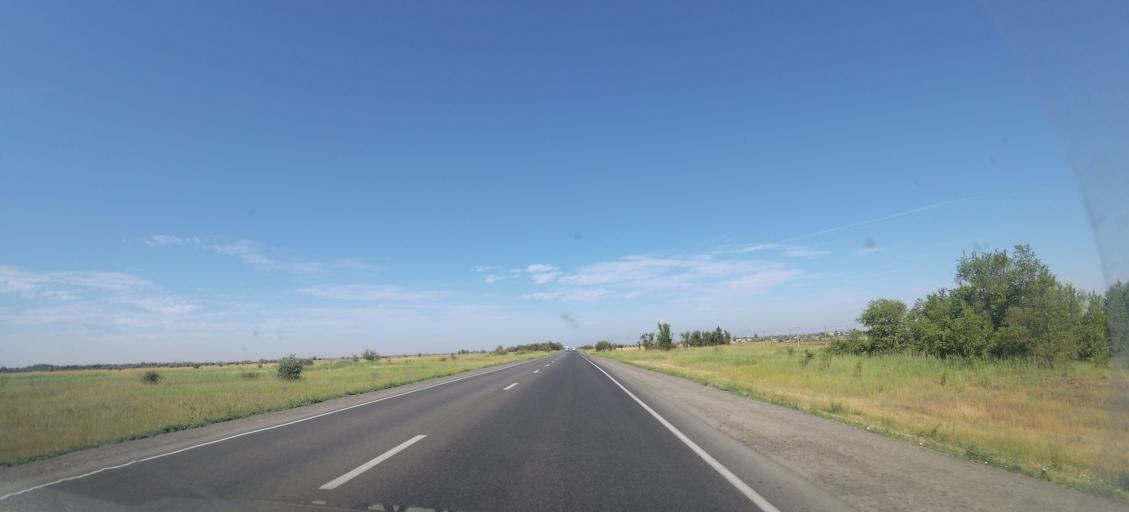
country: RU
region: Volgograd
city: Bereslavka
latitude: 48.6852
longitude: 43.9366
